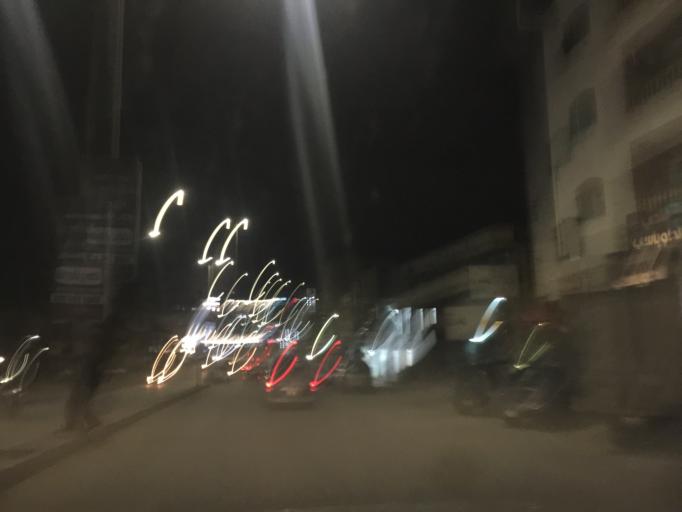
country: JO
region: Zarqa
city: Russeifa
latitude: 32.0255
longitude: 36.0564
